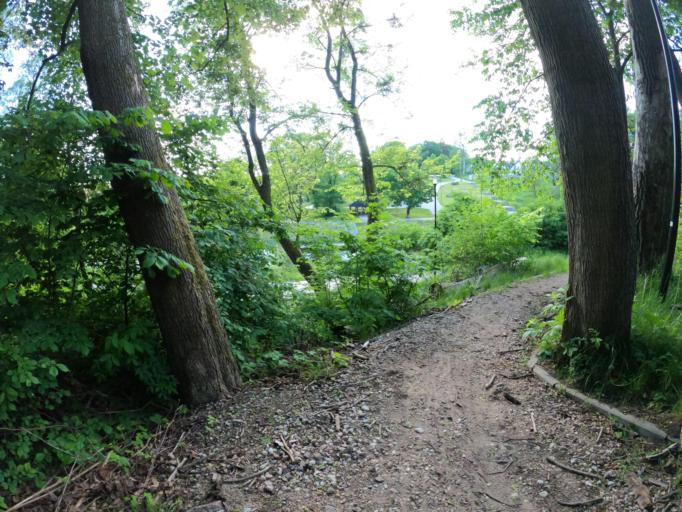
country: PL
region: Warmian-Masurian Voivodeship
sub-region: Powiat lidzbarski
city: Lidzbark Warminski
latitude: 54.1273
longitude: 20.5913
